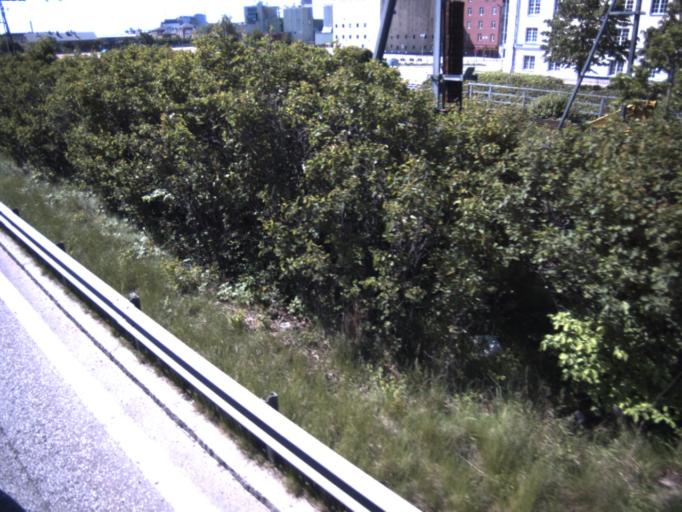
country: SE
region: Skane
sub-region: Helsingborg
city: Helsingborg
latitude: 56.0370
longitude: 12.7017
